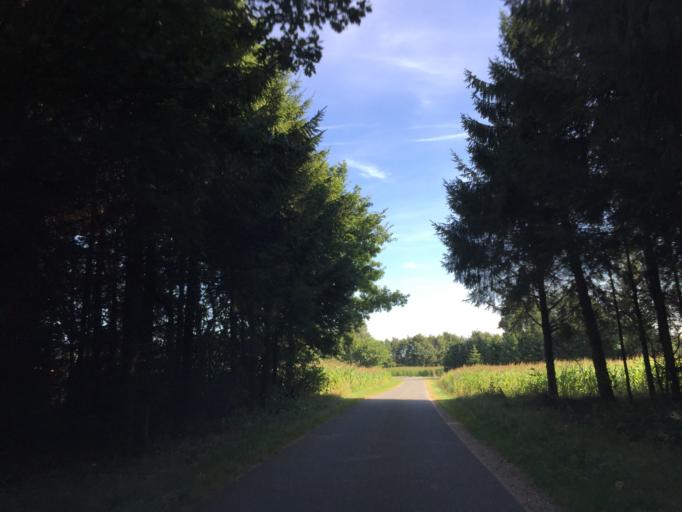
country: DK
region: Central Jutland
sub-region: Viborg Kommune
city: Bjerringbro
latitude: 56.2727
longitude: 9.7040
